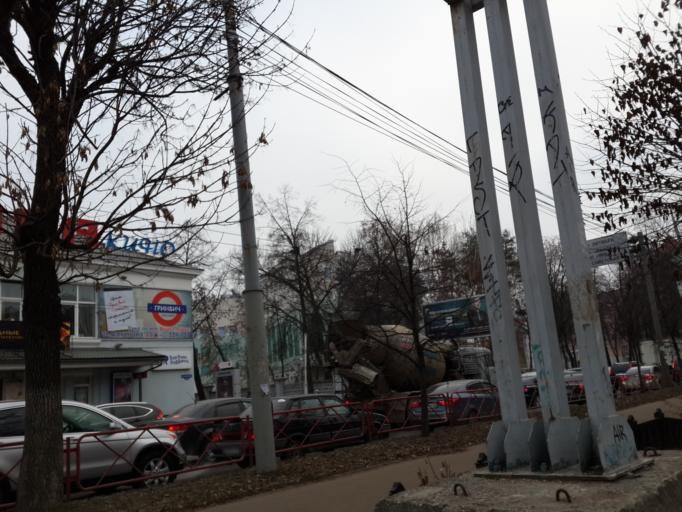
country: RU
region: Jaroslavl
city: Yaroslavl
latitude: 57.6367
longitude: 39.8817
